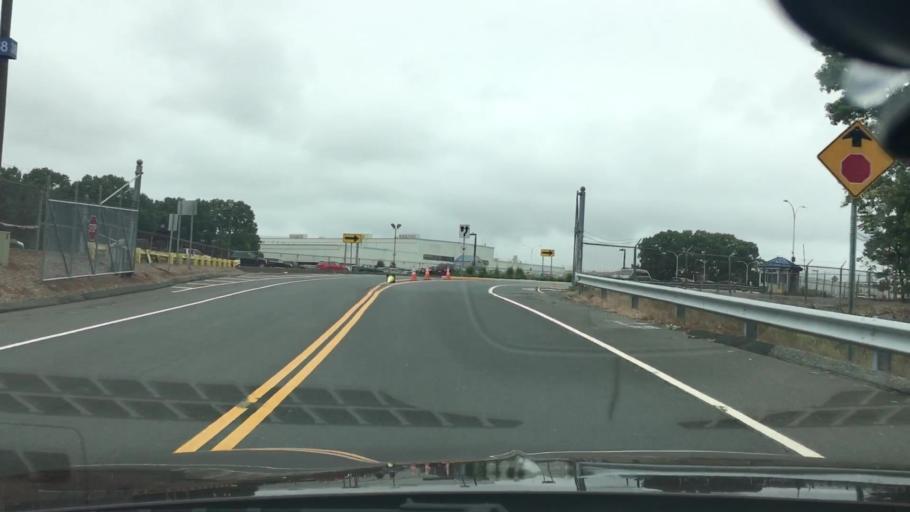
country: US
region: Connecticut
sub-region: Hartford County
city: Windsor Locks
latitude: 41.9213
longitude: -72.6849
